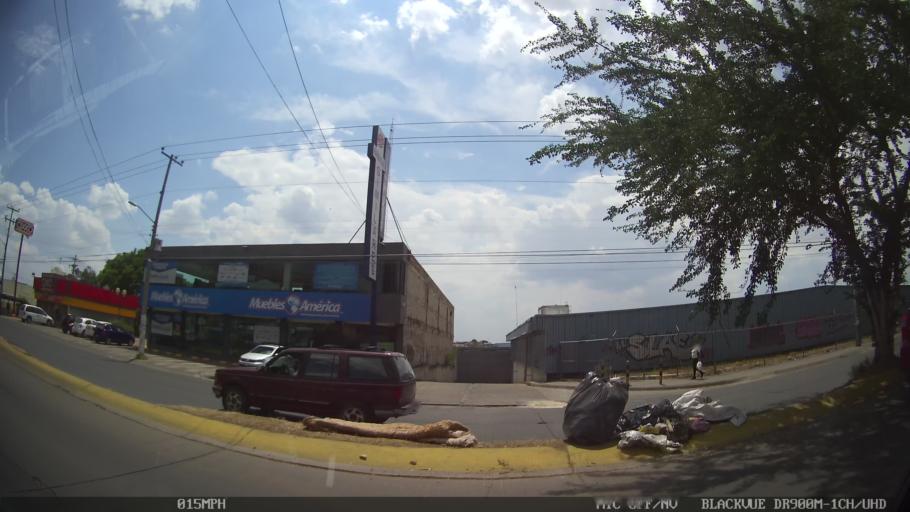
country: MX
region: Jalisco
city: Tlaquepaque
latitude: 20.6388
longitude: -103.2780
